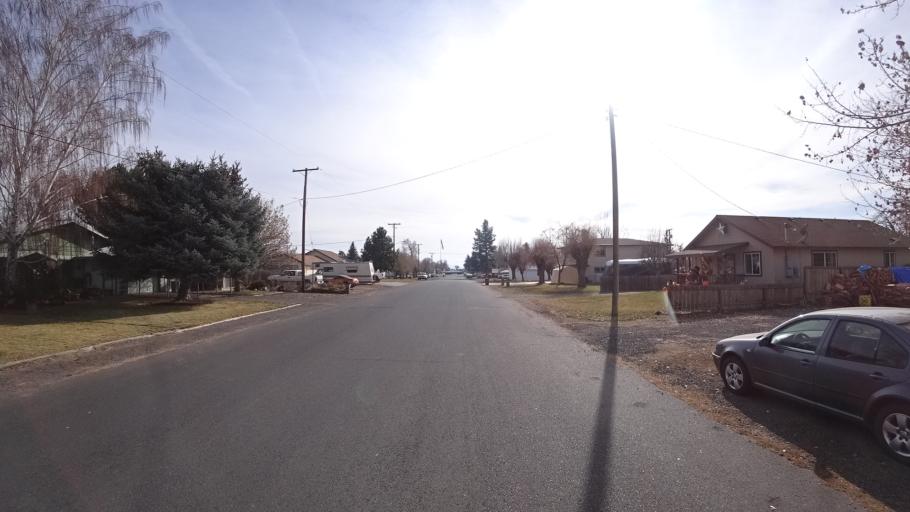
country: US
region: Oregon
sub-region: Klamath County
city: Klamath Falls
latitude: 41.9694
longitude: -121.9184
